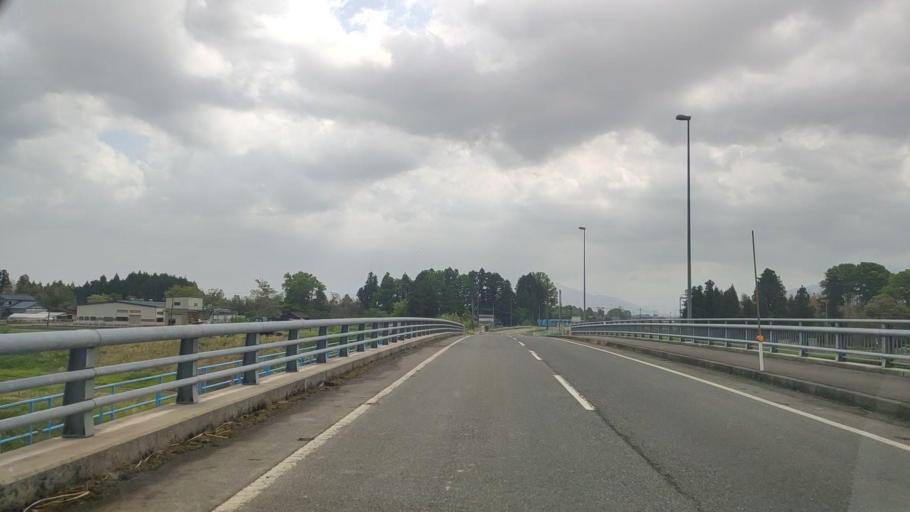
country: JP
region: Niigata
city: Gosen
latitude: 37.7289
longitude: 139.1527
